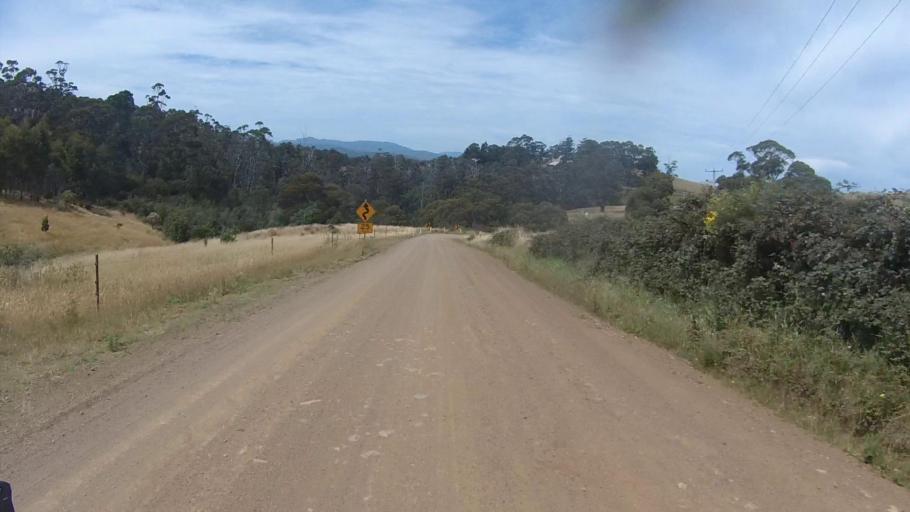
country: AU
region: Tasmania
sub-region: Sorell
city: Sorell
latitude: -42.7852
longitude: 147.8428
